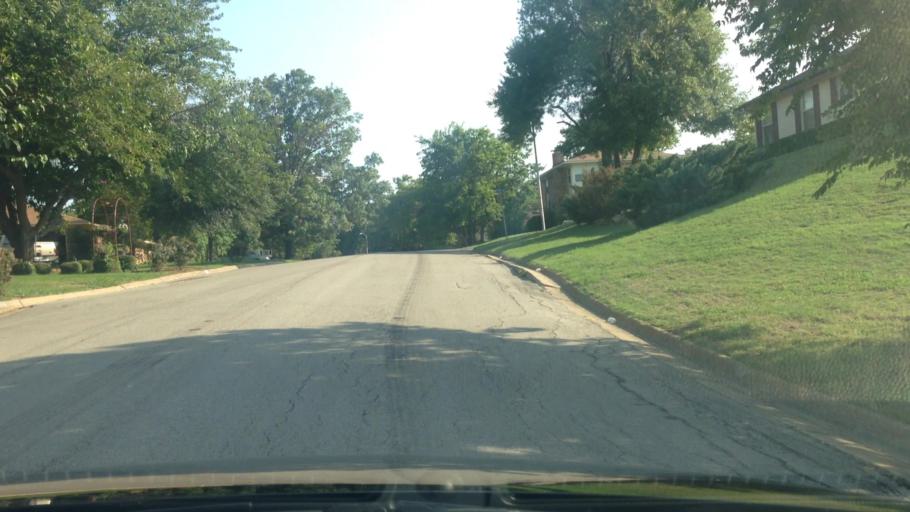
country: US
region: Texas
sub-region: Tarrant County
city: Edgecliff Village
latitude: 32.6574
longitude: -97.3387
